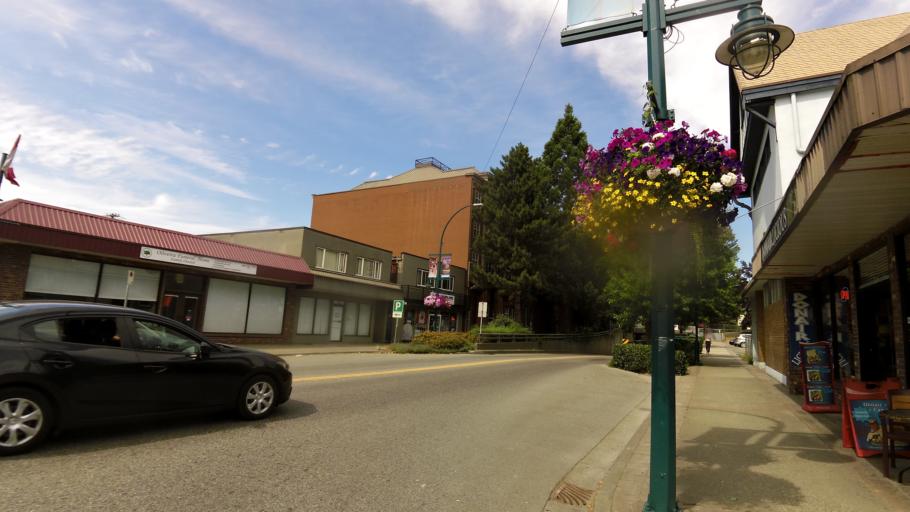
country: CA
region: British Columbia
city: Coquitlam
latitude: 49.2636
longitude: -122.7802
